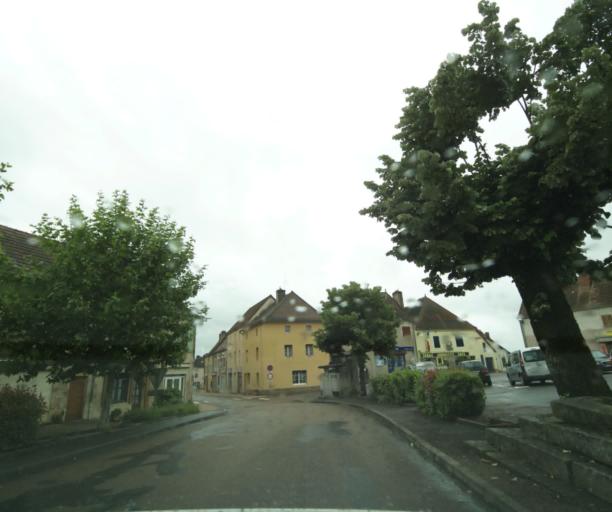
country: FR
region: Bourgogne
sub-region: Departement de Saone-et-Loire
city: Charolles
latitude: 46.4820
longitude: 4.4394
